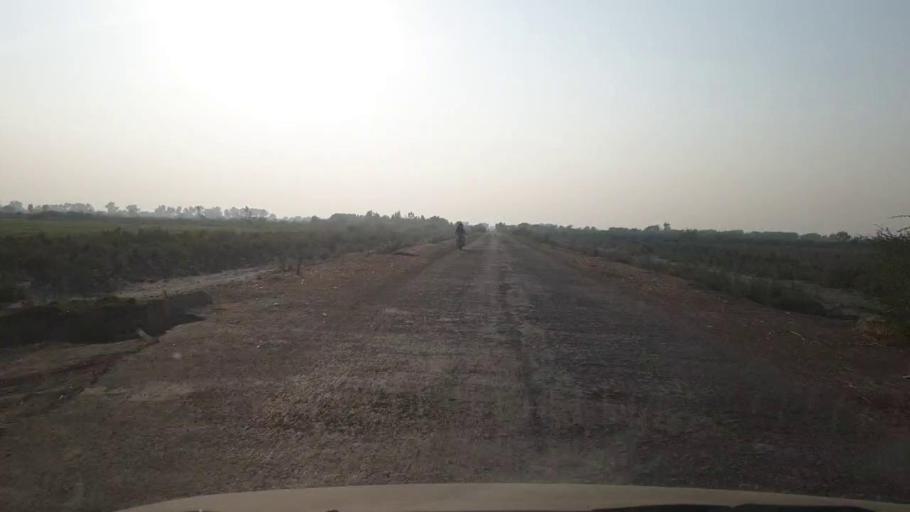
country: PK
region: Sindh
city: Mirwah Gorchani
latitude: 25.3666
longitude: 69.1593
